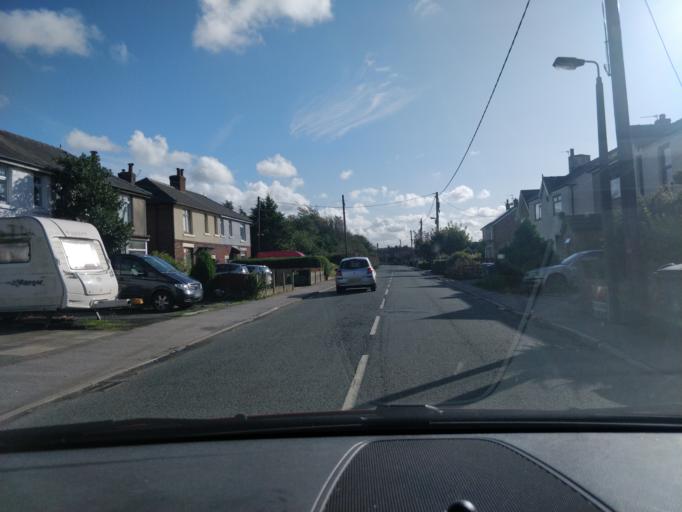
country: GB
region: England
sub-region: Lancashire
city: Banks
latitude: 53.6868
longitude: -2.9137
